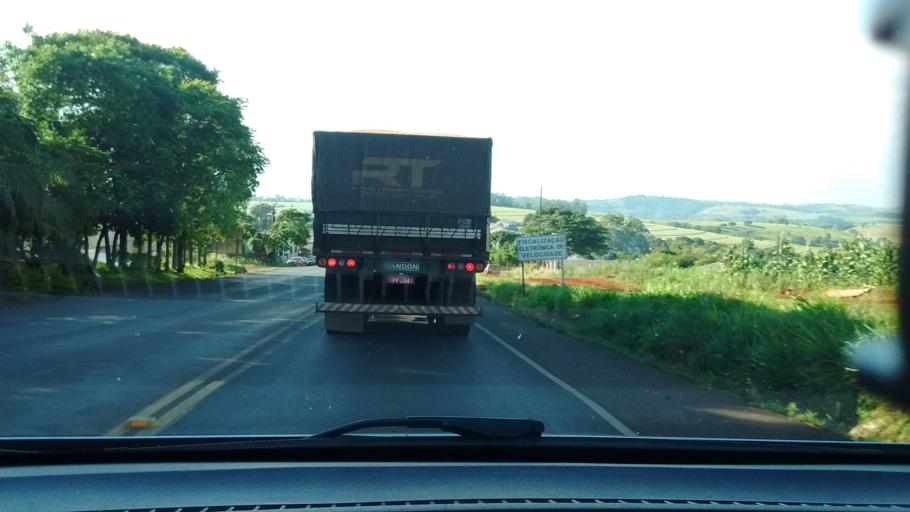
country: BR
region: Parana
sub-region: Cascavel
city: Cascavel
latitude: -25.2542
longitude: -53.5772
